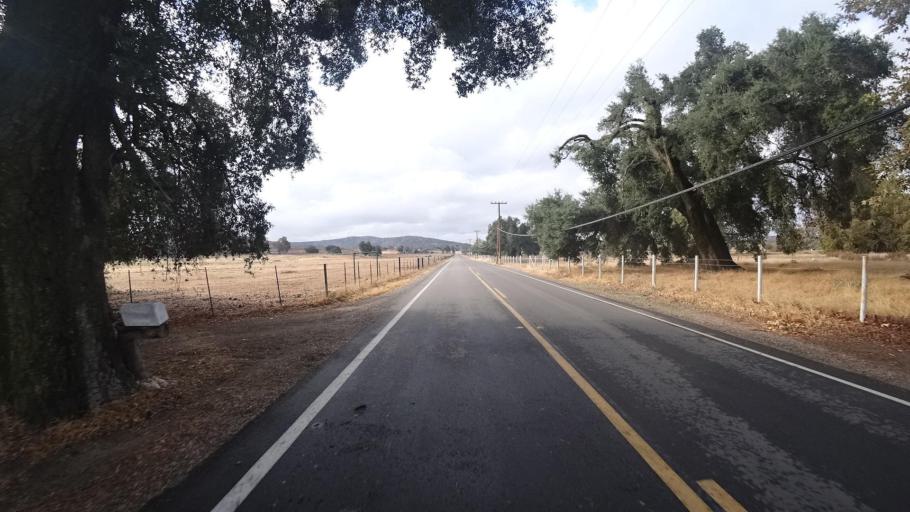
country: MX
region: Baja California
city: Tecate
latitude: 32.6207
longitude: -116.6134
